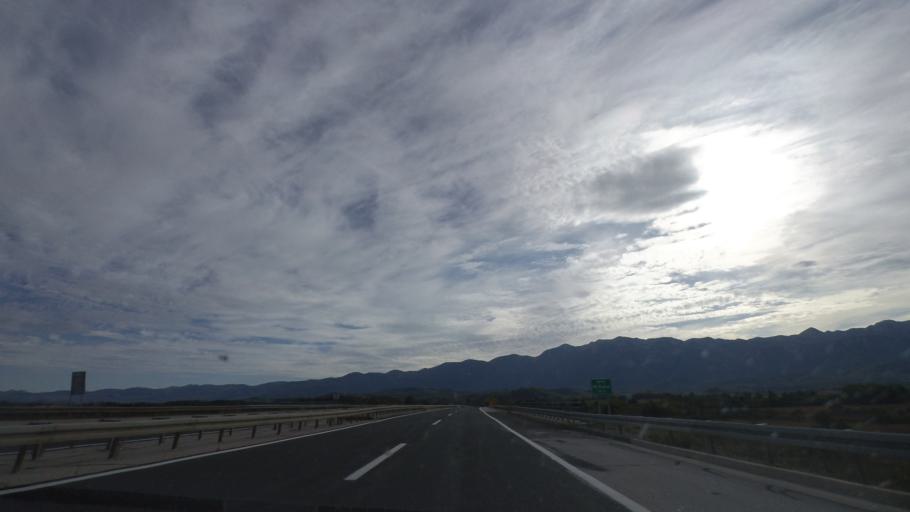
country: HR
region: Zadarska
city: Obrovac
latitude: 44.4005
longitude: 15.6358
